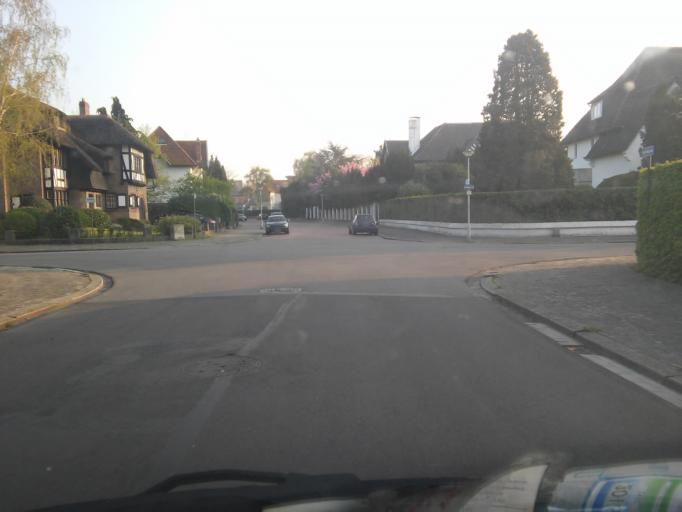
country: BE
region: Flanders
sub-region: Provincie Antwerpen
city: Antwerpen
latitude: 51.1777
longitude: 4.4032
